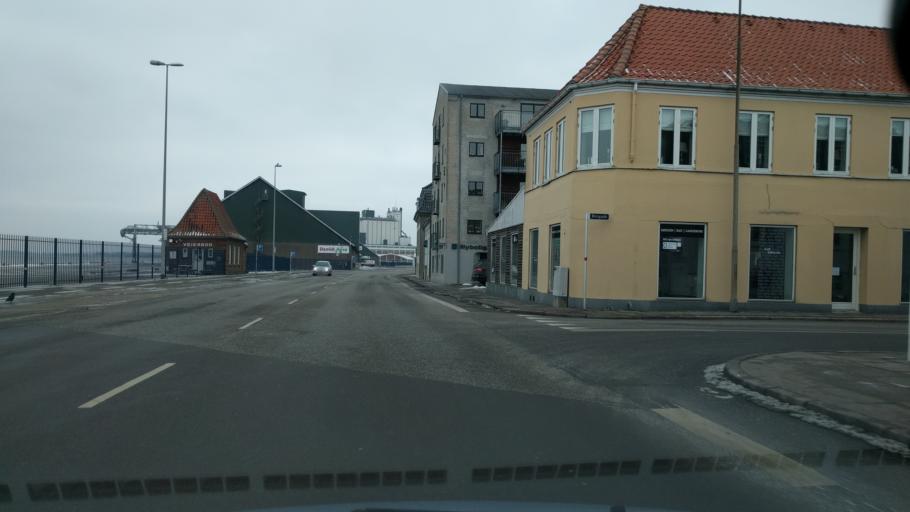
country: DK
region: Zealand
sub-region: Guldborgsund Kommune
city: Nykobing Falster
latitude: 54.7651
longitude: 11.8654
